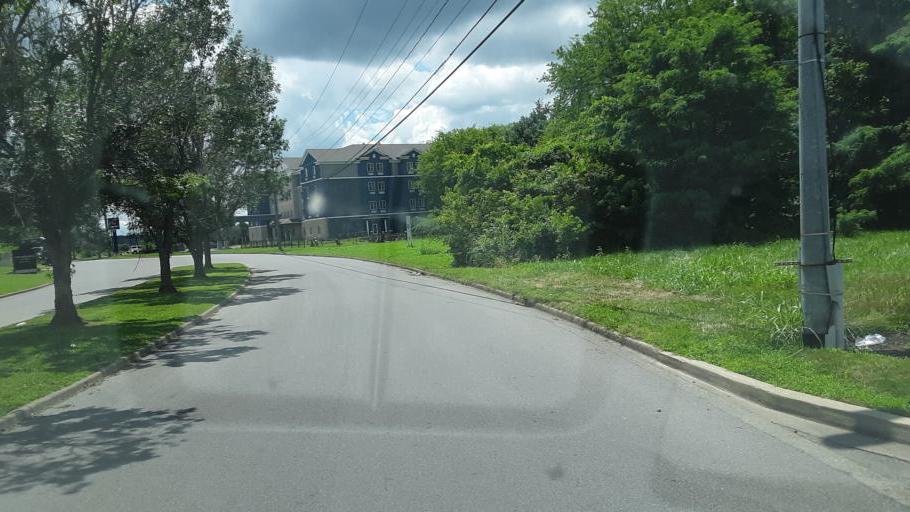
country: US
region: Tennessee
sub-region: Montgomery County
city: Clarksville
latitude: 36.5978
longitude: -87.2894
